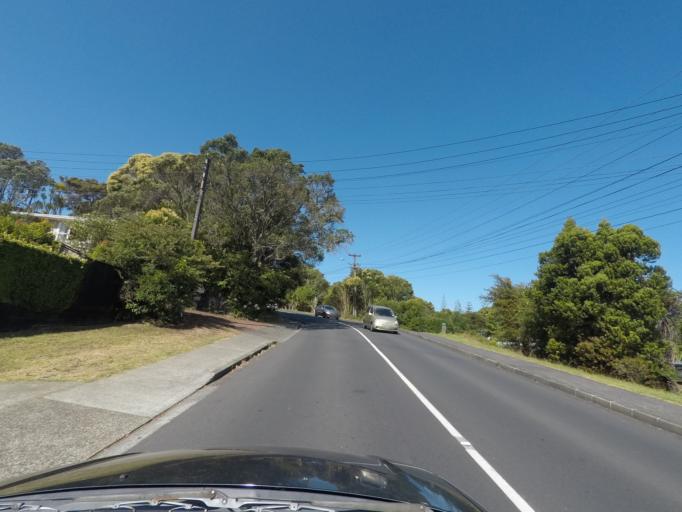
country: NZ
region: Auckland
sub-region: Auckland
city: Waitakere
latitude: -36.9222
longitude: 174.6586
